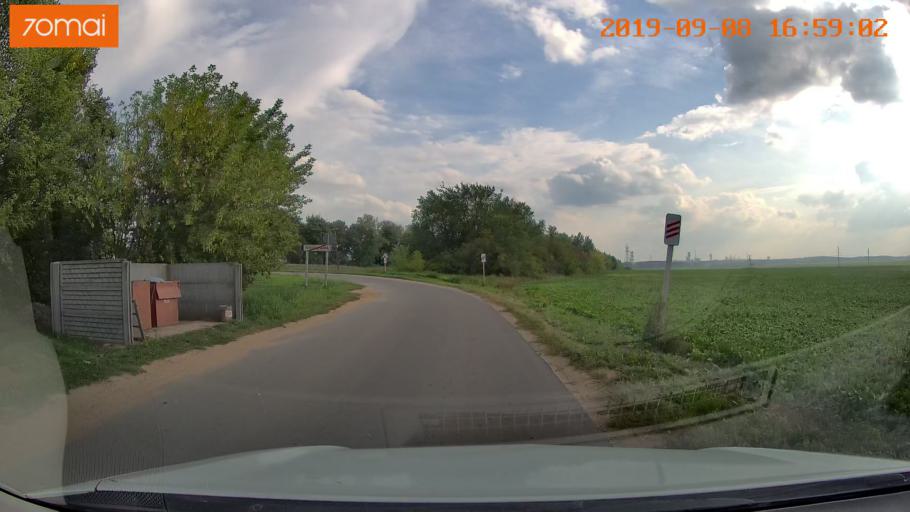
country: BY
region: Grodnenskaya
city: Hrodna
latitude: 53.7239
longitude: 23.9328
